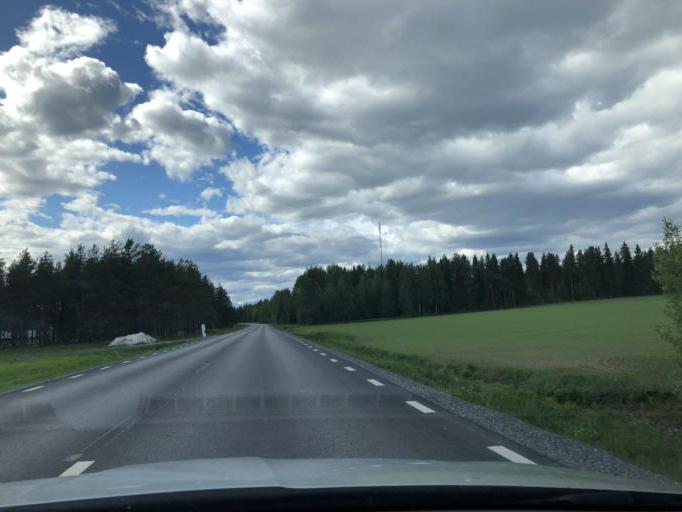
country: SE
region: Norrbotten
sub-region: Alvsbyns Kommun
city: AElvsbyn
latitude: 65.6761
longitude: 20.8322
